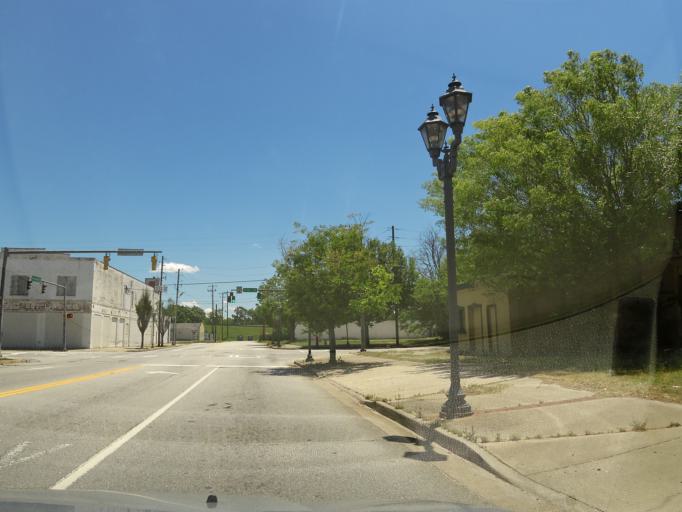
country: US
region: Georgia
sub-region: Richmond County
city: Augusta
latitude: 33.4744
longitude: -81.9588
